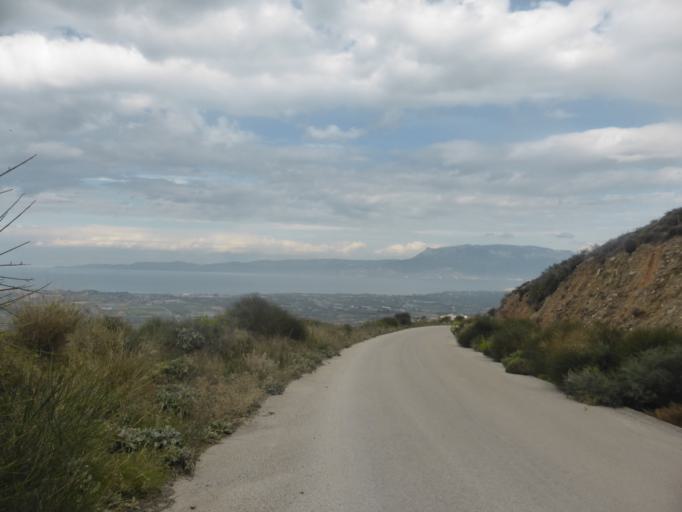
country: GR
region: Peloponnese
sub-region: Nomos Korinthias
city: Arkhaia Korinthos
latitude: 37.8938
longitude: 22.8688
